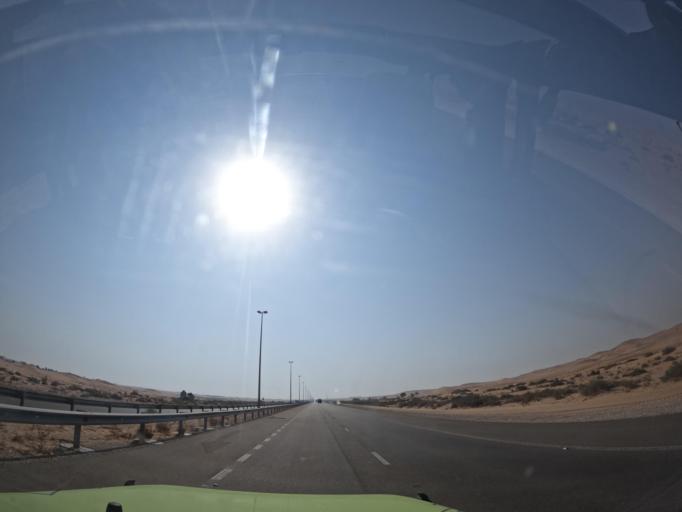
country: OM
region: Al Buraimi
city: Al Buraymi
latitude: 24.5154
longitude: 55.5603
